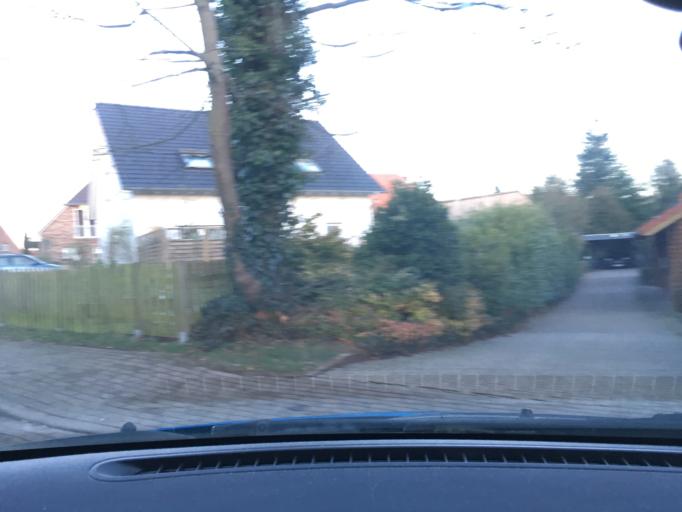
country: DE
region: Lower Saxony
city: Handeloh
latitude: 53.2438
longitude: 9.8419
